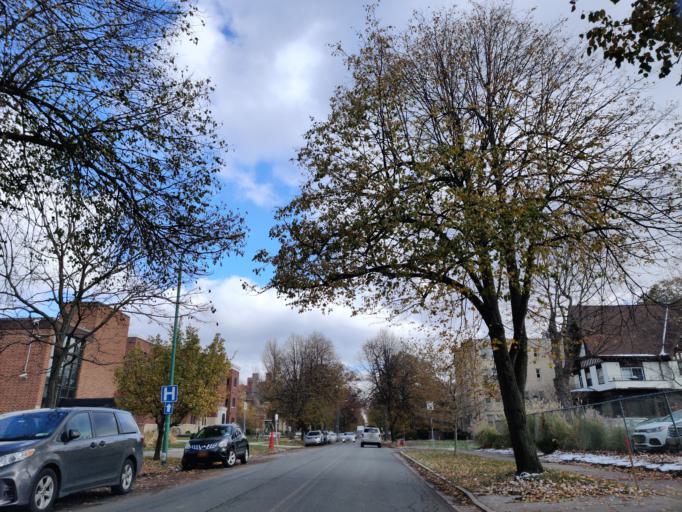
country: US
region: New York
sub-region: Erie County
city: Buffalo
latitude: 42.9023
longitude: -78.8809
